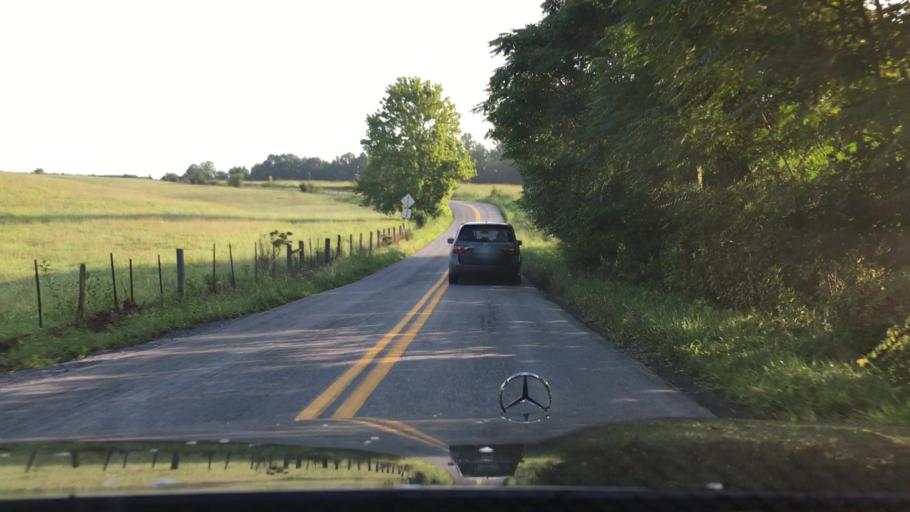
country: US
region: Virginia
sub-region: Campbell County
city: Timberlake
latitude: 37.2845
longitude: -79.2728
